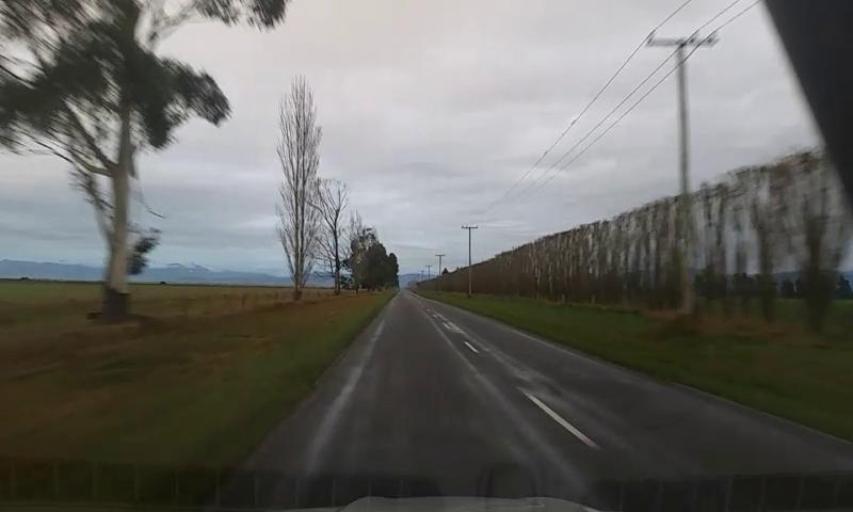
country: NZ
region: Canterbury
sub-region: Ashburton District
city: Methven
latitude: -43.7395
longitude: 171.6811
